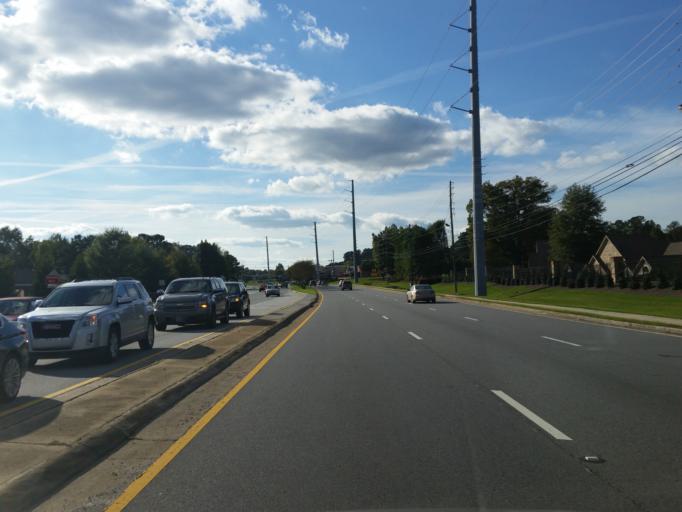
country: US
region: Georgia
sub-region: Cobb County
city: Kennesaw
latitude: 33.9533
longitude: -84.6494
